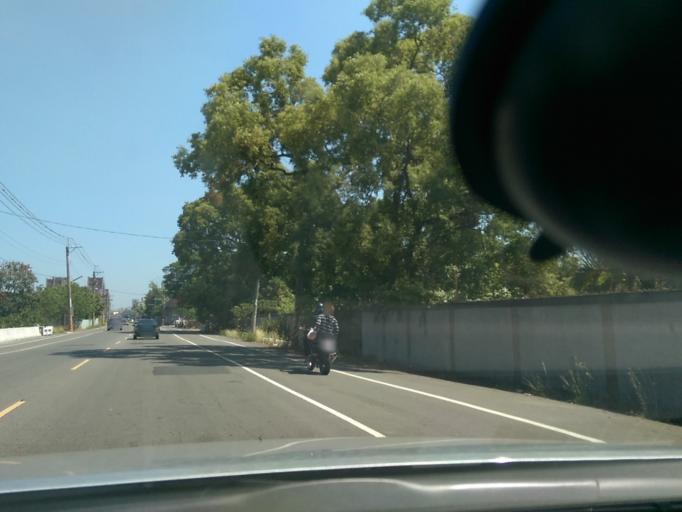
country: TW
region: Taiwan
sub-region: Chiayi
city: Jiayi Shi
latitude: 23.4400
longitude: 120.4541
